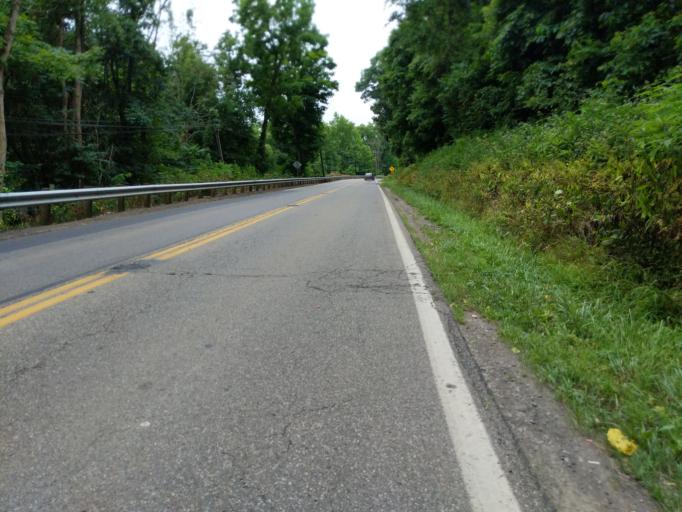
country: US
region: Ohio
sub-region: Athens County
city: Chauncey
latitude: 39.3927
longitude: -82.1409
